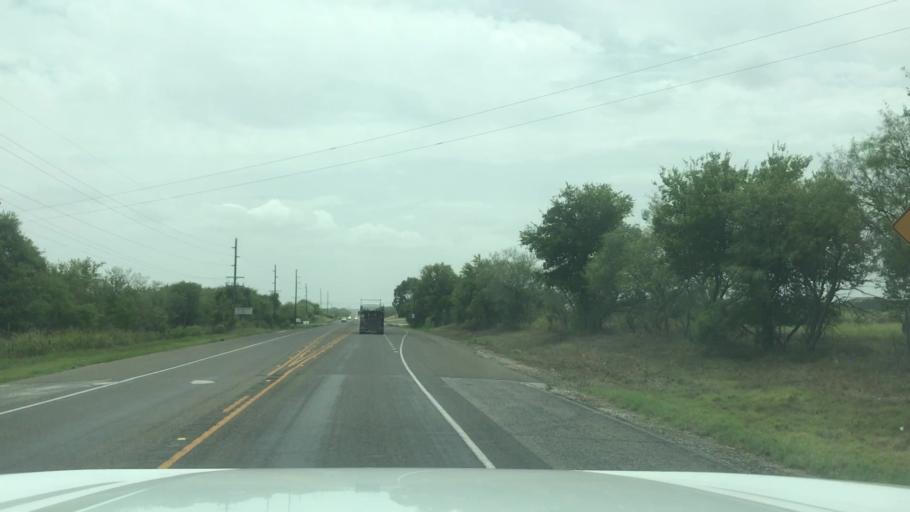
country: US
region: Texas
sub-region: Bosque County
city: Clifton
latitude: 31.7345
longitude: -97.5511
